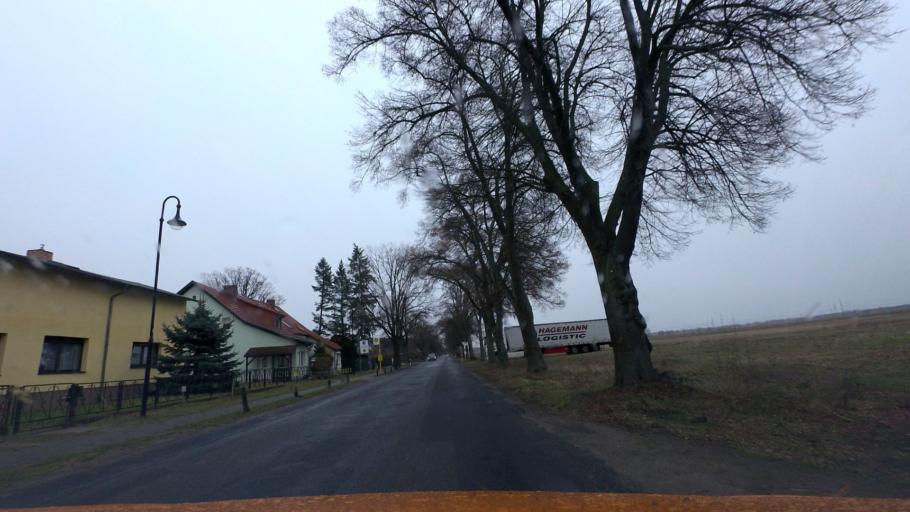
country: DE
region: Brandenburg
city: Brieselang
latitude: 52.6372
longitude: 13.0492
